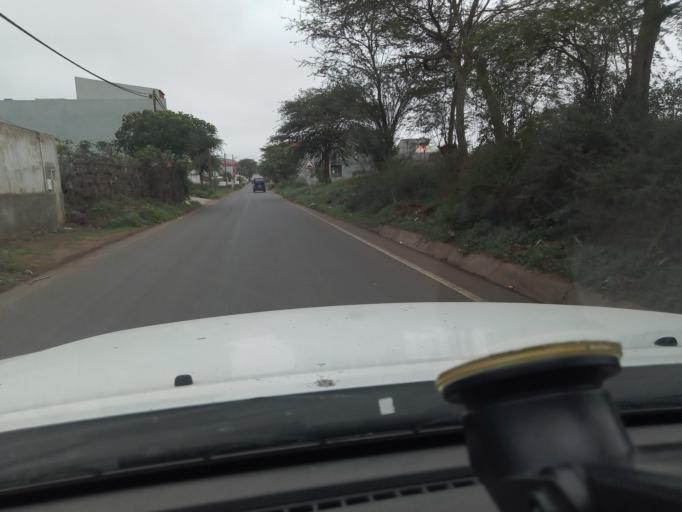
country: CV
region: Santa Catarina
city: Assomada
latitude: 15.1282
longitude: -23.6726
